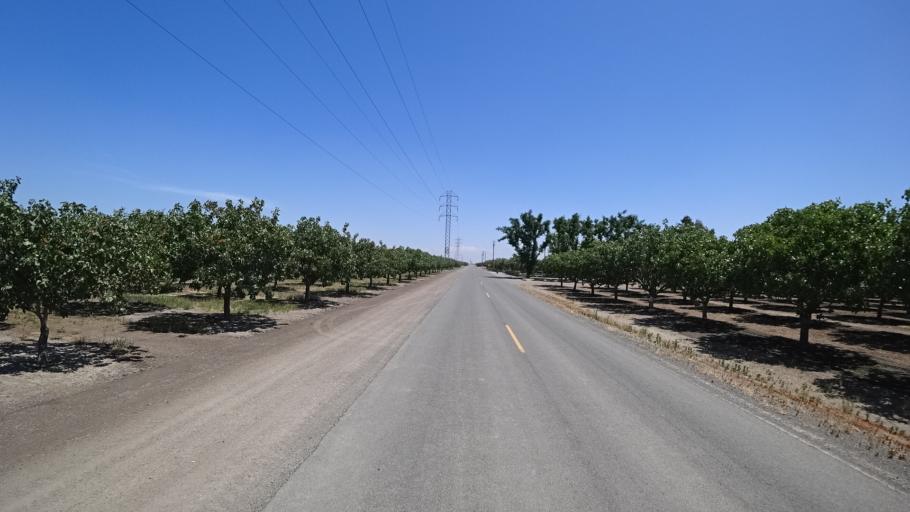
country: US
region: California
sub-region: Kings County
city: Corcoran
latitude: 36.1090
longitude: -119.5398
